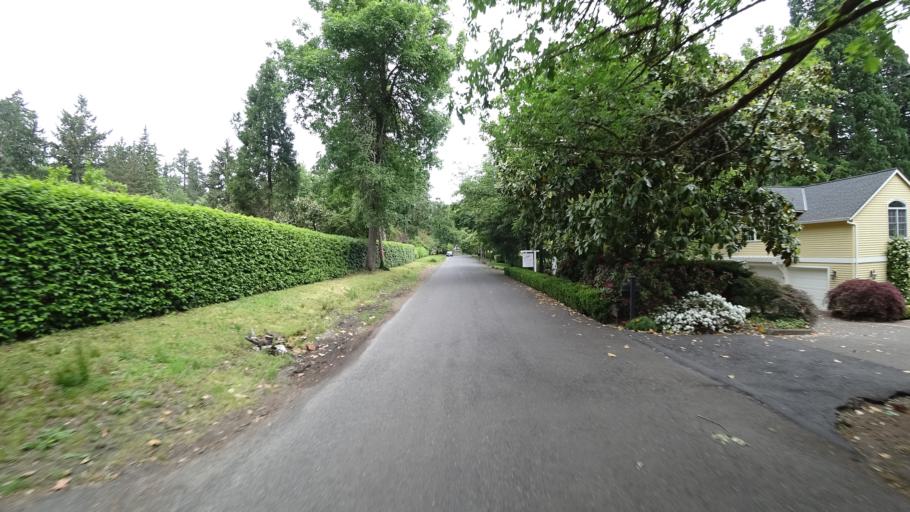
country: US
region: Oregon
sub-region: Clackamas County
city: Lake Oswego
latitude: 45.4347
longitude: -122.6588
